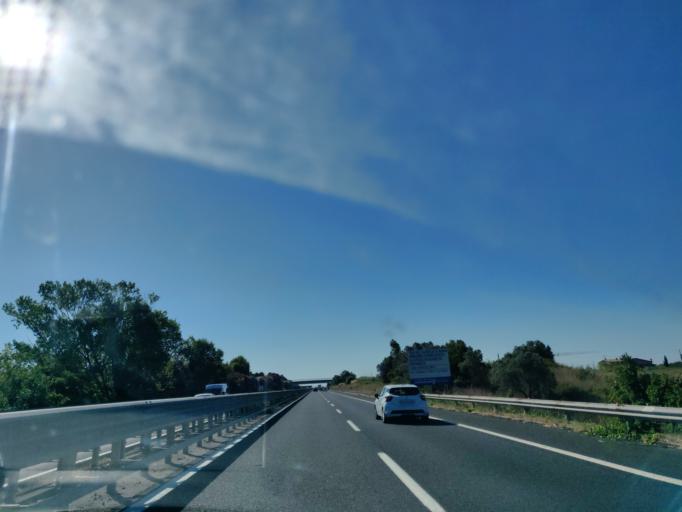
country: IT
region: Latium
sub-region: Citta metropolitana di Roma Capitale
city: Cerveteri
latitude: 41.9751
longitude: 12.0952
